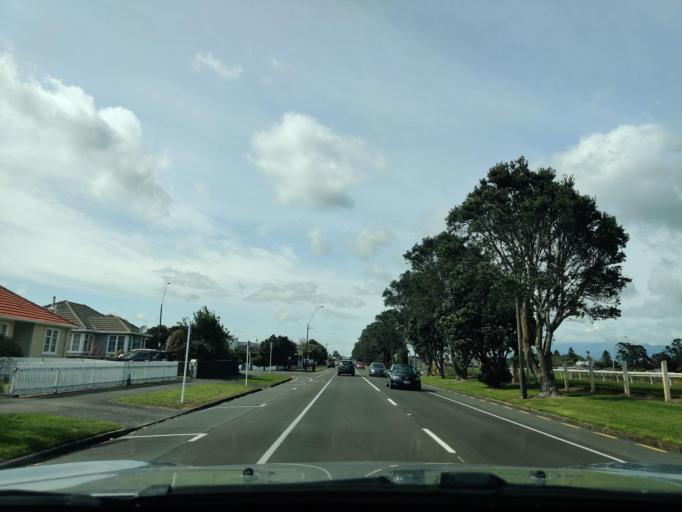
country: NZ
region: Taranaki
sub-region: New Plymouth District
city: New Plymouth
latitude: -39.0652
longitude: 174.0878
